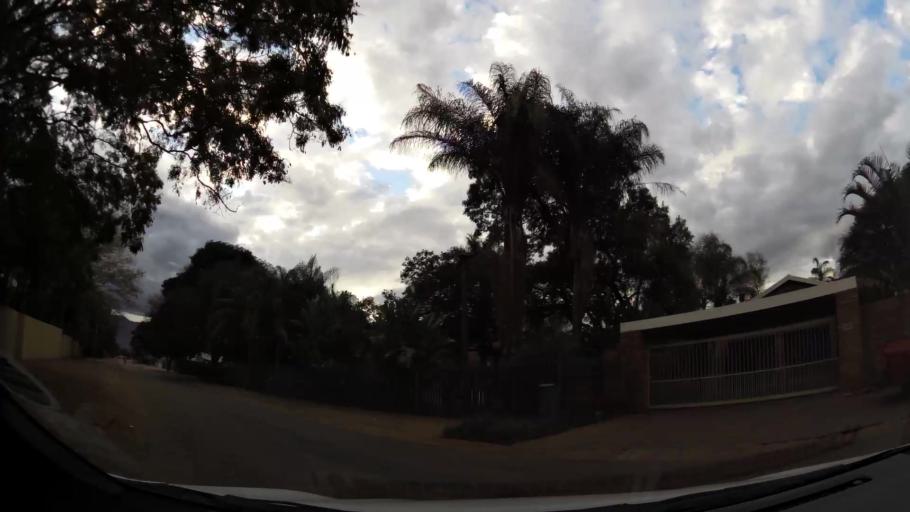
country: ZA
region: Limpopo
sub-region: Waterberg District Municipality
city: Mokopane
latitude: -24.1995
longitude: 29.0049
